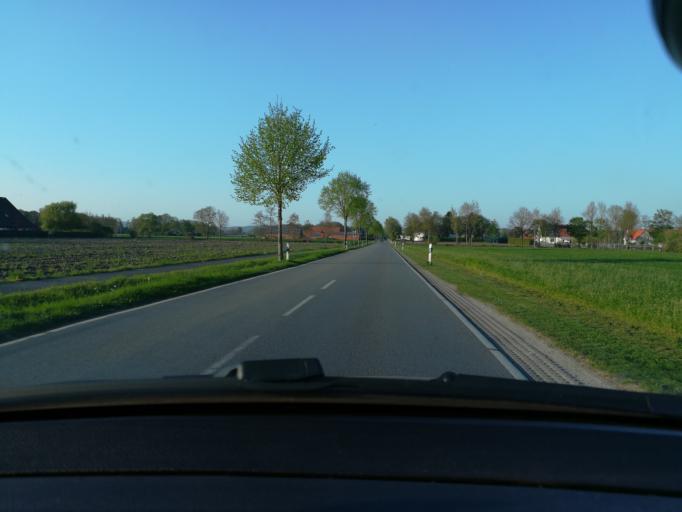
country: DE
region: North Rhine-Westphalia
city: Versmold
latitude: 52.0576
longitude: 8.1827
